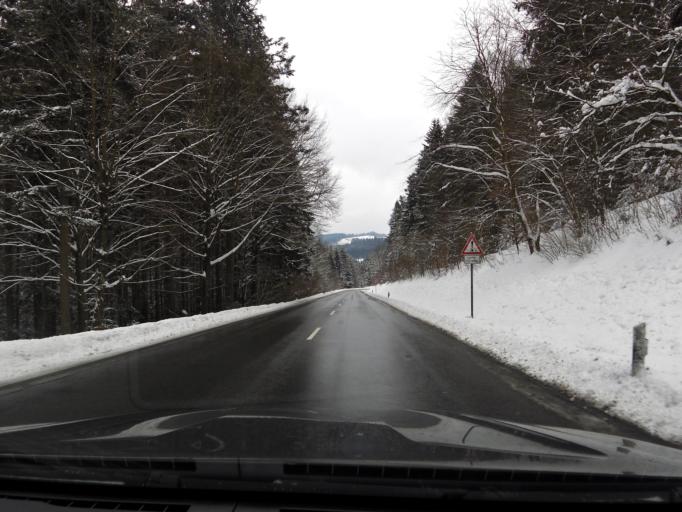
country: DE
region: Bavaria
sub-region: Lower Bavaria
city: Innernzell
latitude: 48.8587
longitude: 13.2986
